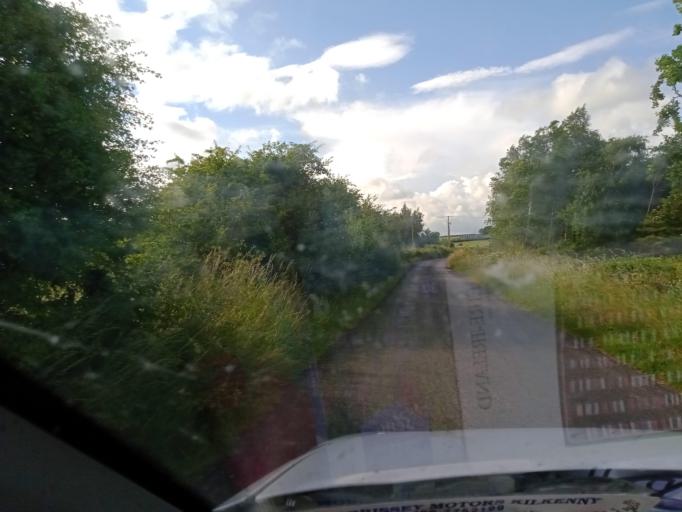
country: IE
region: Leinster
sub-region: Laois
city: Rathdowney
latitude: 52.7824
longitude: -7.5463
